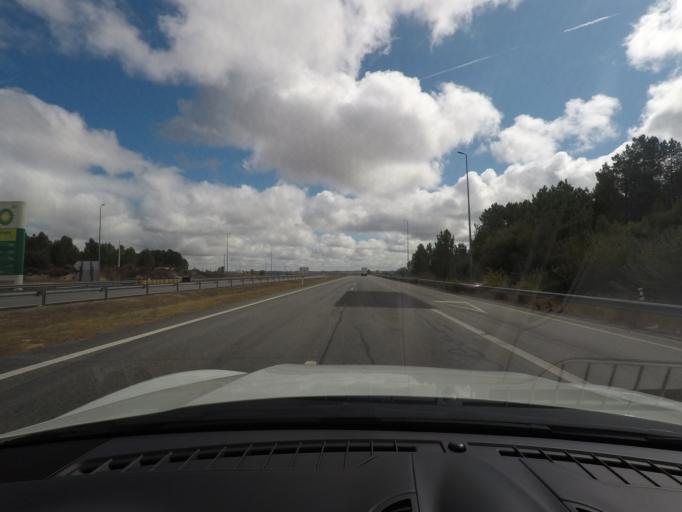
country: ES
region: Castille and Leon
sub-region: Provincia de Salamanca
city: Fuentes de Onoro
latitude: 40.6043
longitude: -6.9509
